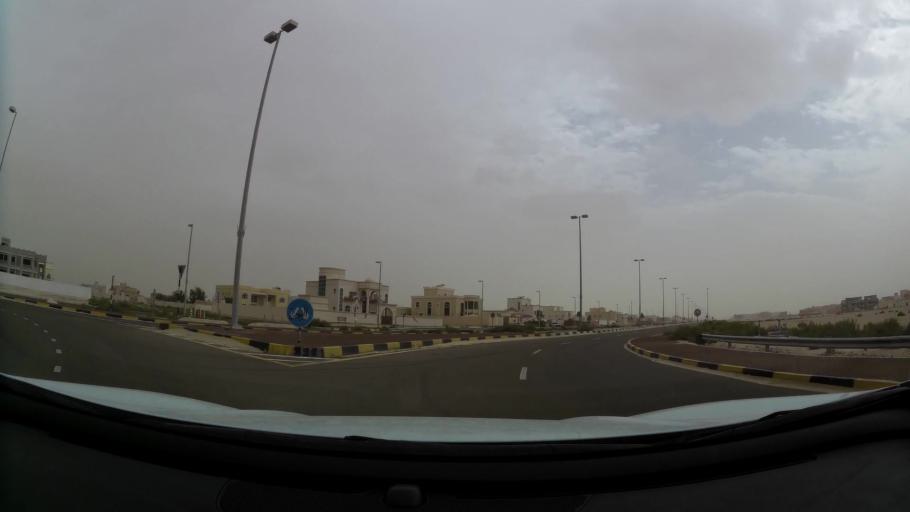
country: AE
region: Abu Dhabi
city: Abu Dhabi
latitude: 24.3644
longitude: 54.6948
